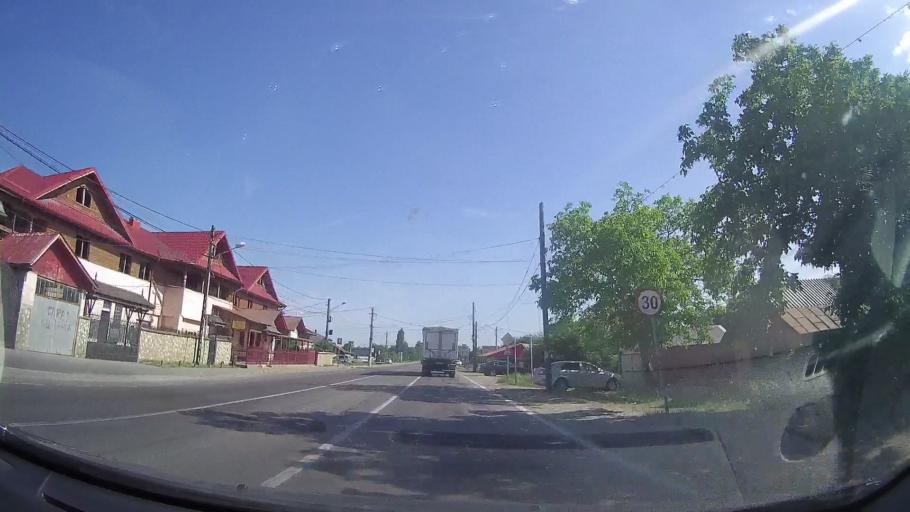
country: RO
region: Prahova
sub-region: Comuna Lipanesti
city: Sipotu
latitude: 45.0296
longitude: 26.0183
